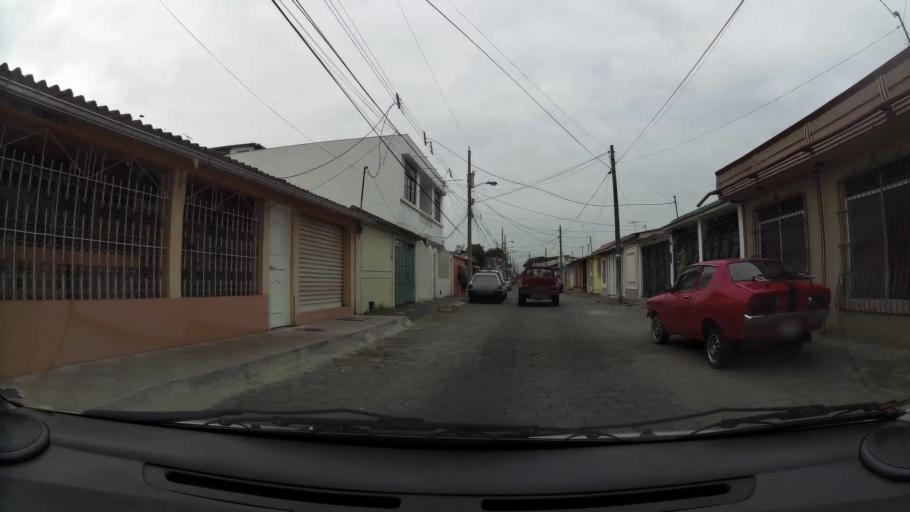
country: EC
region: Guayas
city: Eloy Alfaro
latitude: -2.1348
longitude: -79.9002
